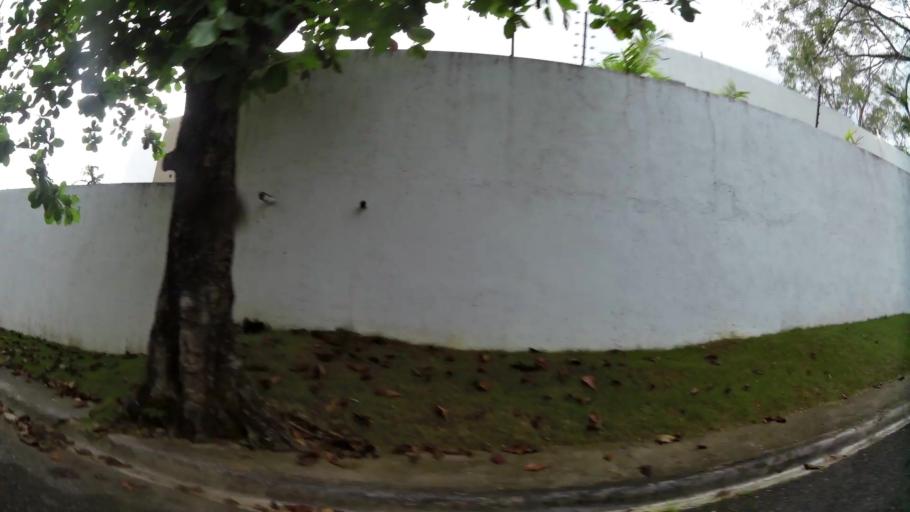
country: DO
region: Nacional
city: La Agustina
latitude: 18.5128
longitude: -69.9449
